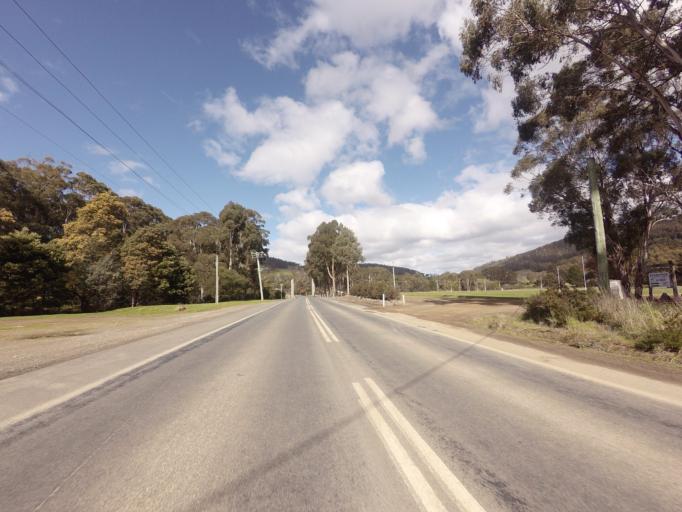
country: AU
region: Tasmania
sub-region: Huon Valley
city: Geeveston
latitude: -43.1650
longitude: 146.9390
